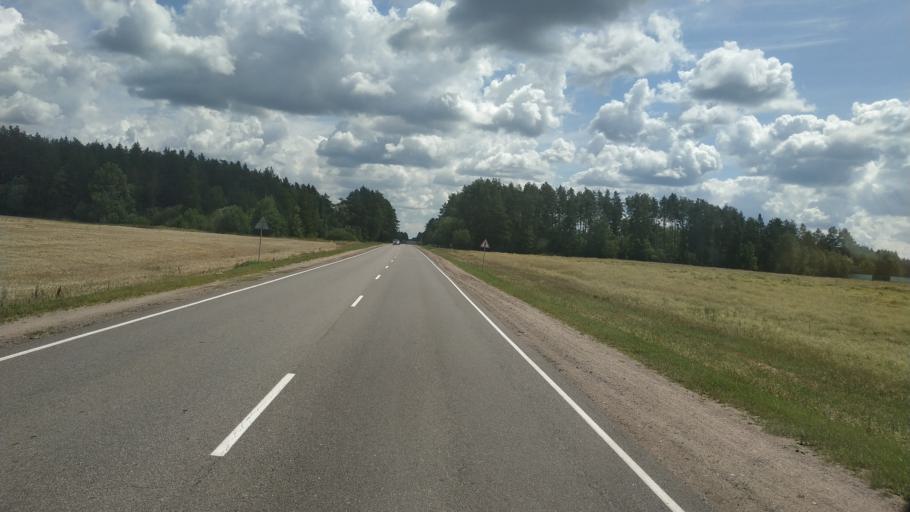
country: BY
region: Mogilev
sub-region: Mahilyowski Rayon
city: Veyno
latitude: 53.8312
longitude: 30.4065
